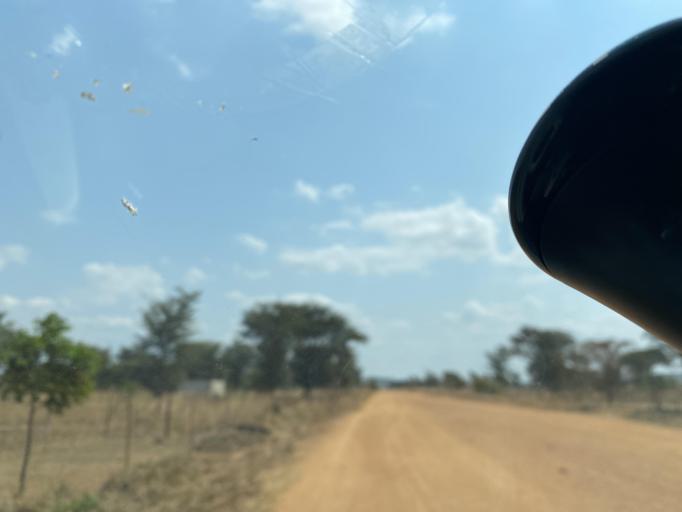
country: ZM
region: Lusaka
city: Chongwe
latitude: -15.5892
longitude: 28.7610
